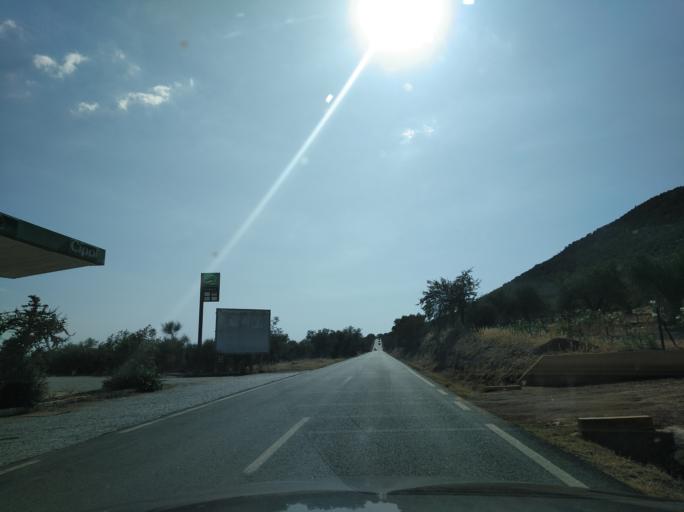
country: ES
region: Andalusia
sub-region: Provincia de Huelva
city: Rosal de la Frontera
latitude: 37.9590
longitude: -7.2577
